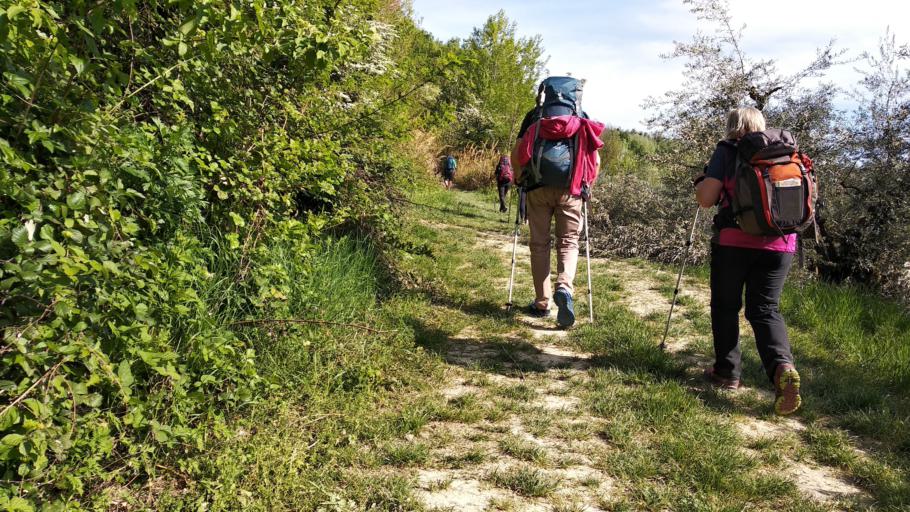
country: IT
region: Emilia-Romagna
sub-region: Provincia di Ravenna
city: Fognano
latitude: 44.2264
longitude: 11.7217
